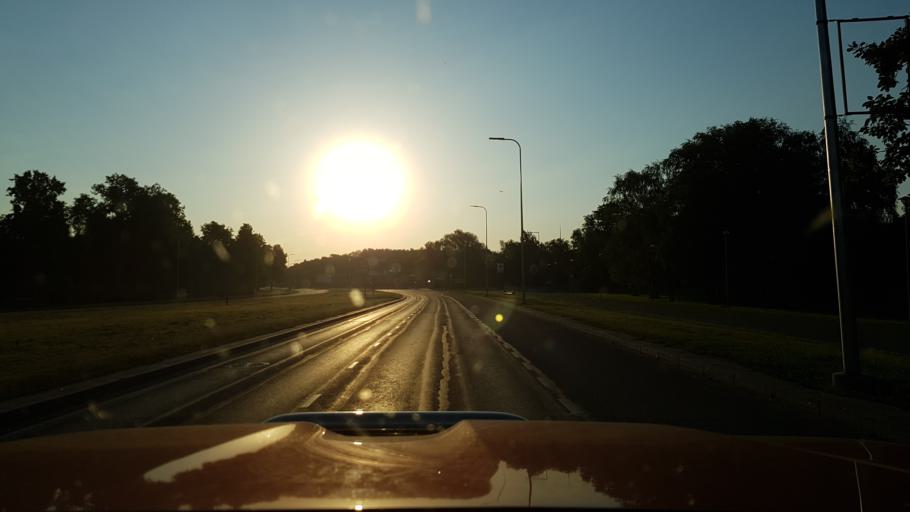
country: EE
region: Harju
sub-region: Viimsi vald
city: Viimsi
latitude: 59.4612
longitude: 24.8216
